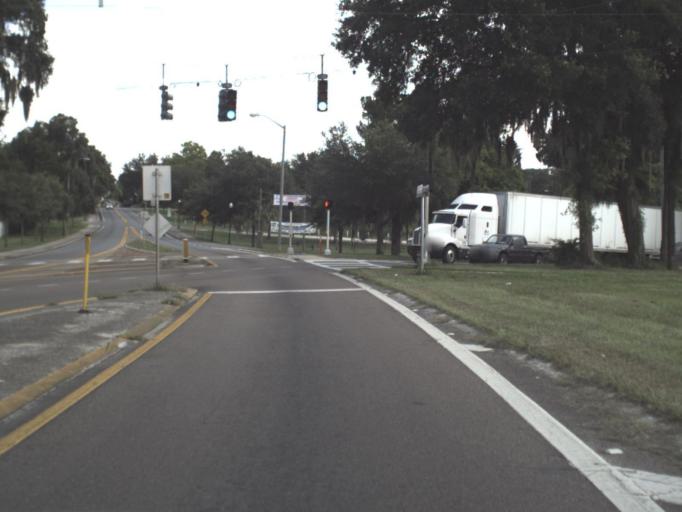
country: US
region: Florida
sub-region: Pasco County
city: Dade City
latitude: 28.3547
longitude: -82.1875
